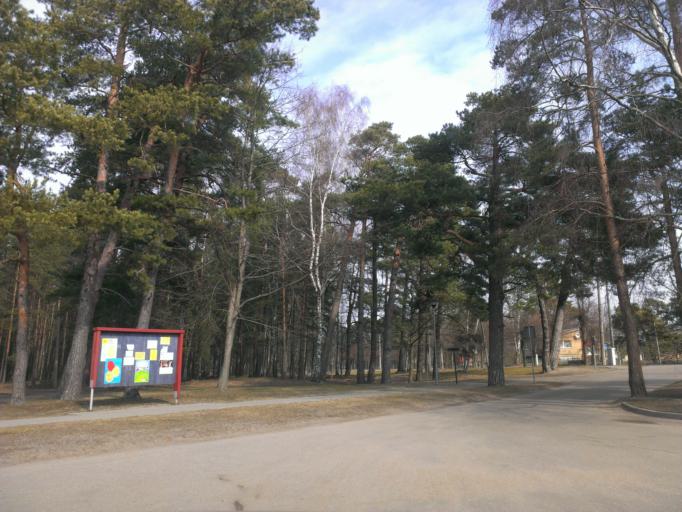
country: LV
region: Salacgrivas
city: Ainazi
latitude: 57.8592
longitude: 24.3565
